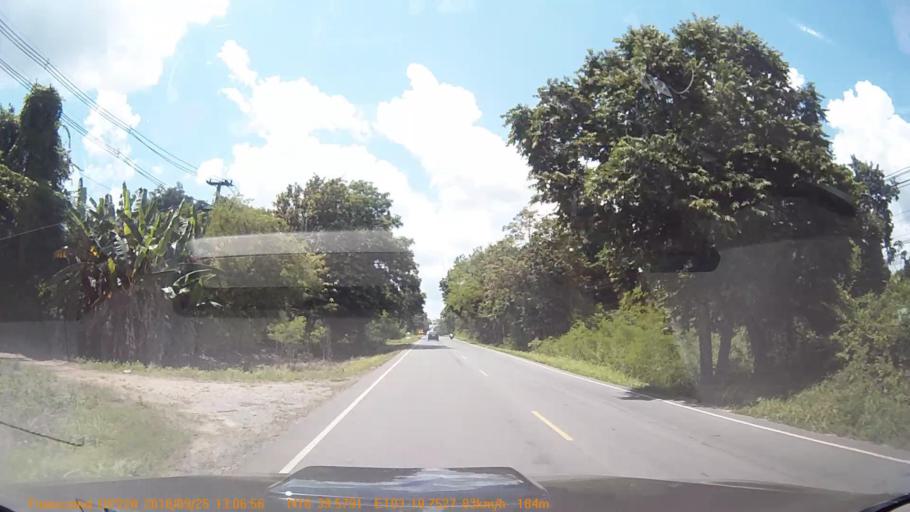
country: TH
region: Kalasin
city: Huai Mek
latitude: 16.6597
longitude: 103.1791
